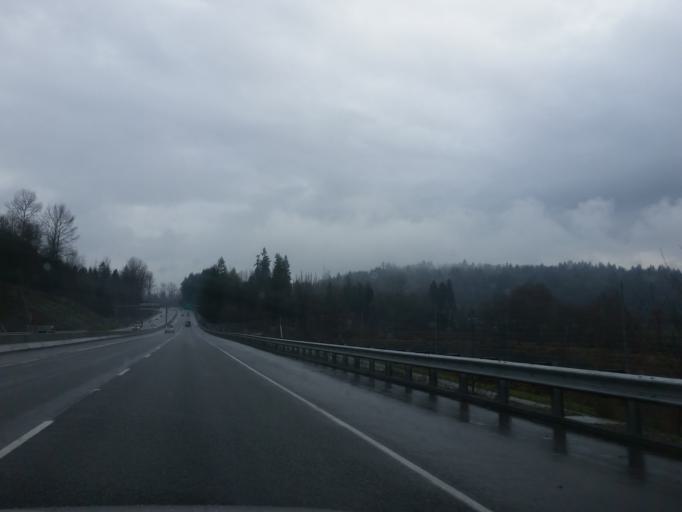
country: US
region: Washington
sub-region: Snohomish County
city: Monroe
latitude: 47.8317
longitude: -122.0264
